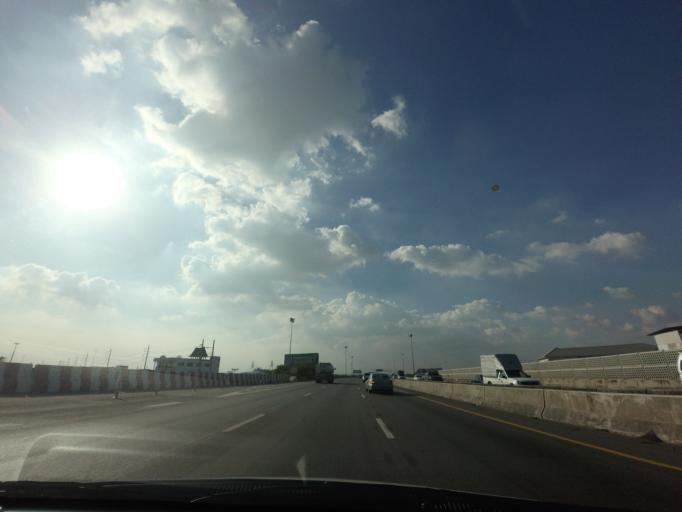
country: TH
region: Samut Prakan
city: Phra Samut Chedi
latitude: 13.6332
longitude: 100.5715
